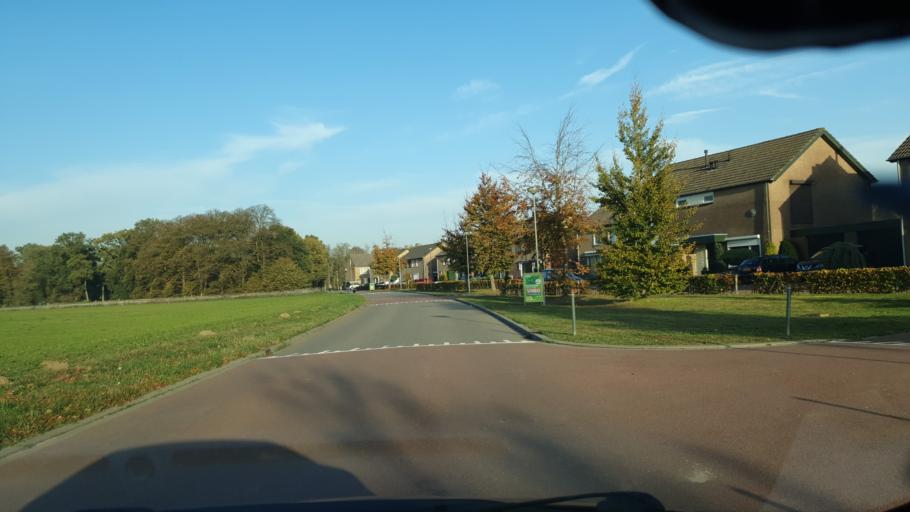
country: NL
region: Limburg
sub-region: Gemeente Roerdalen
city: Sint Odilienberg
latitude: 51.1425
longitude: 5.9929
